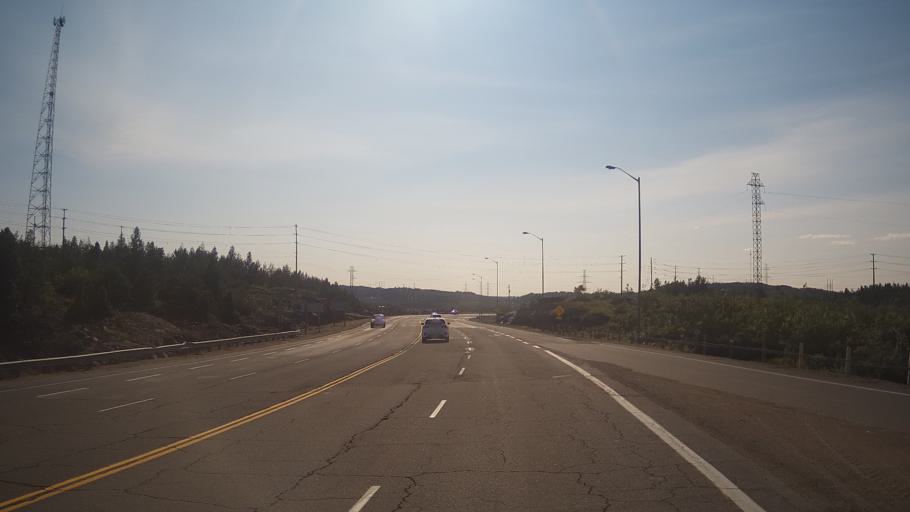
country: CA
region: Ontario
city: Greater Sudbury
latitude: 46.5028
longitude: -81.0366
